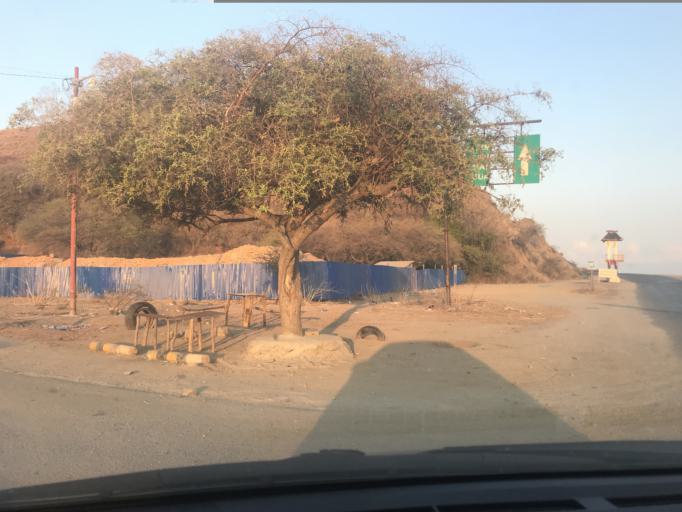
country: TL
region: Dili
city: Dili
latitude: -8.5572
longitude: 125.4988
